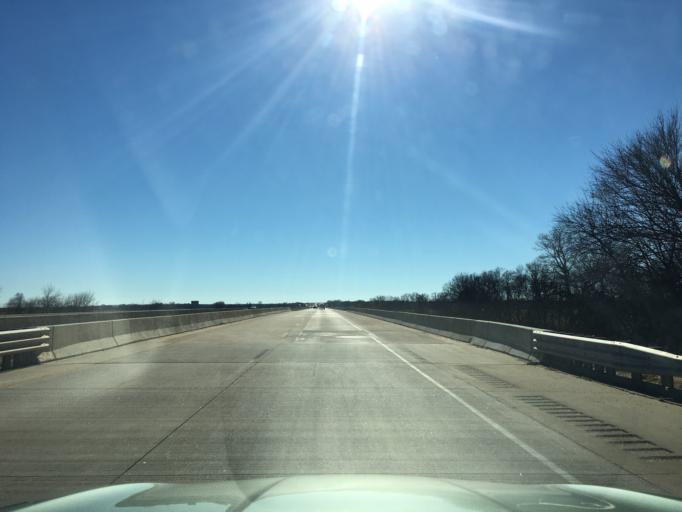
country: US
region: Oklahoma
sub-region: Noble County
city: Perry
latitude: 36.4770
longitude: -97.3272
